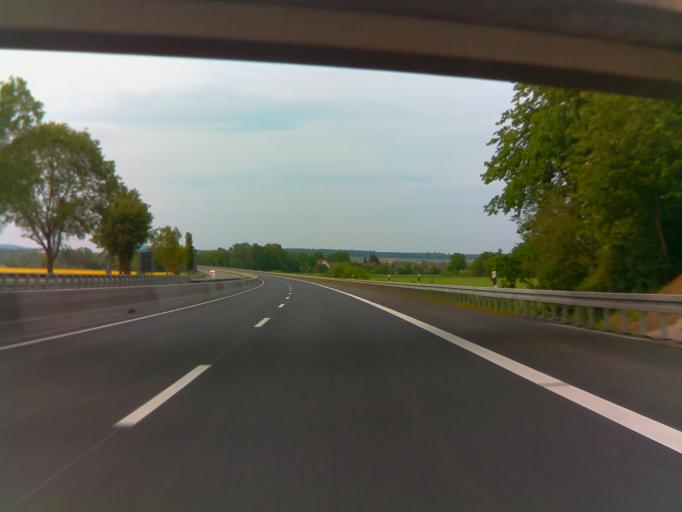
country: DE
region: Hesse
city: Fritzlar
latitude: 51.1041
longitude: 9.2968
